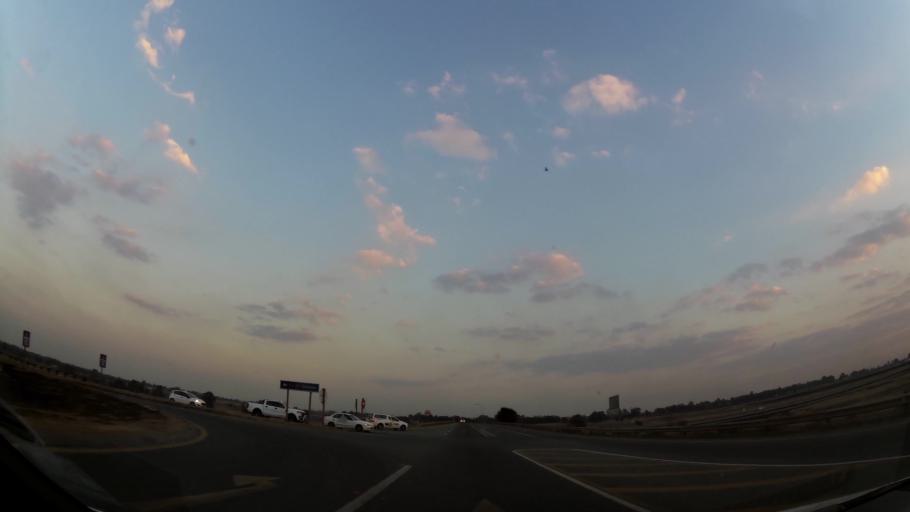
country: ZA
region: Gauteng
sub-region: Ekurhuleni Metropolitan Municipality
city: Springs
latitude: -26.2828
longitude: 28.4295
